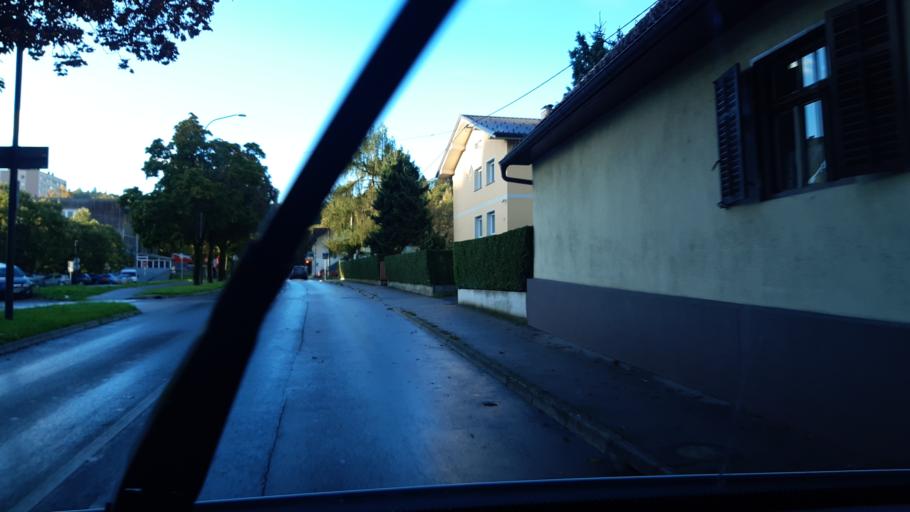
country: SI
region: Ljubljana
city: Ljubljana
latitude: 46.0493
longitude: 14.5430
